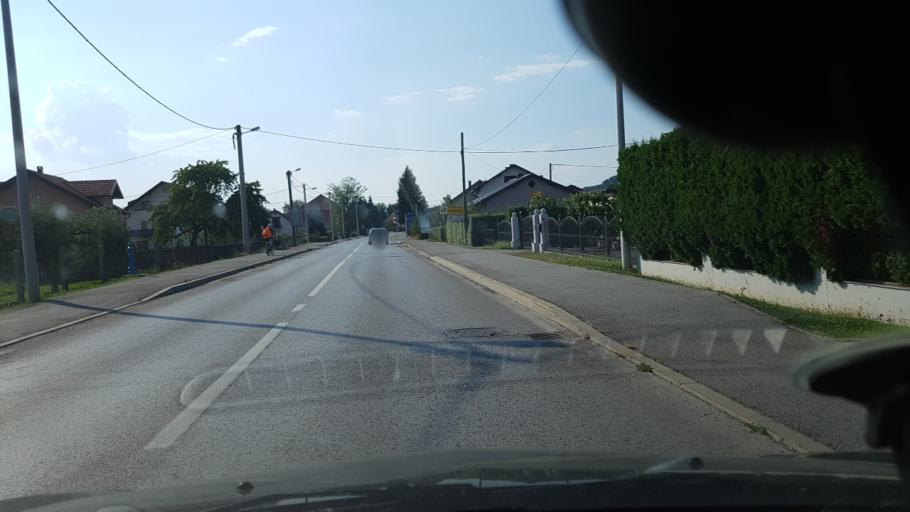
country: HR
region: Zagrebacka
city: Brdovec
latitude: 45.8637
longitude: 15.7726
